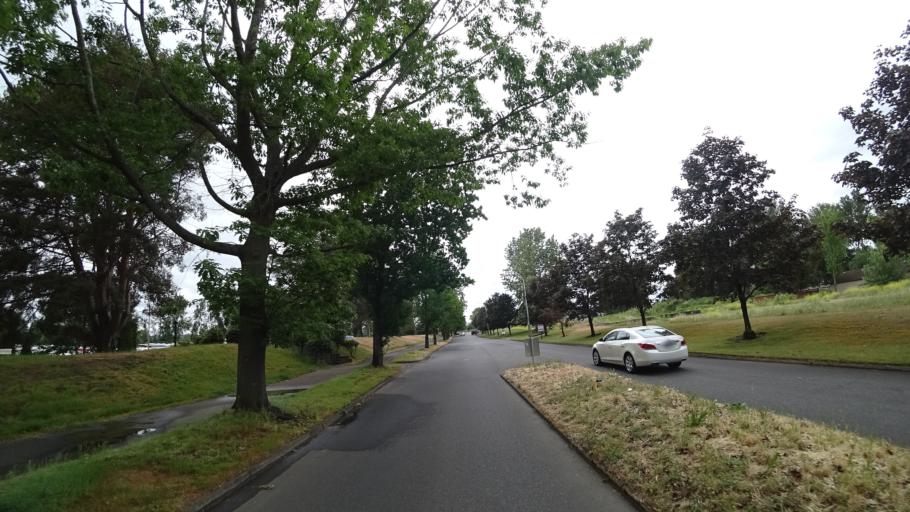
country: US
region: Washington
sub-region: Clark County
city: Vancouver
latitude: 45.6062
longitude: -122.6680
